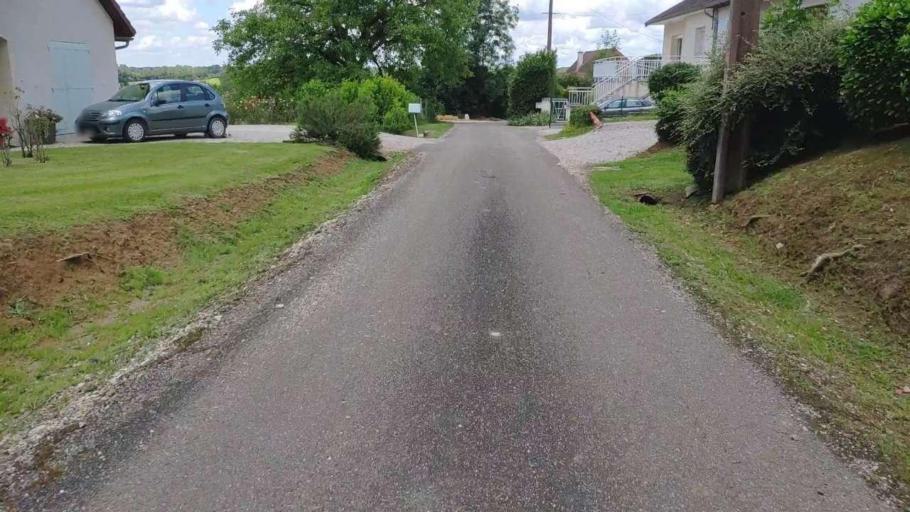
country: FR
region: Franche-Comte
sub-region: Departement du Jura
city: Bletterans
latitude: 46.8493
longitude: 5.4668
